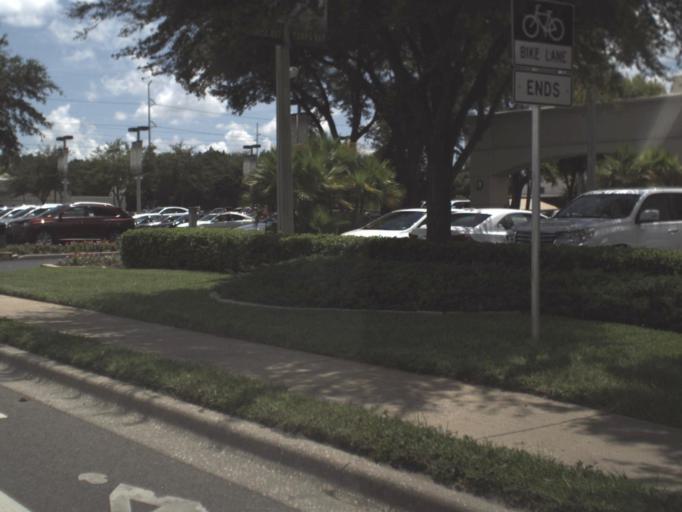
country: US
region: Florida
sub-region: Hillsborough County
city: Egypt Lake-Leto
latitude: 28.0014
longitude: -82.5053
